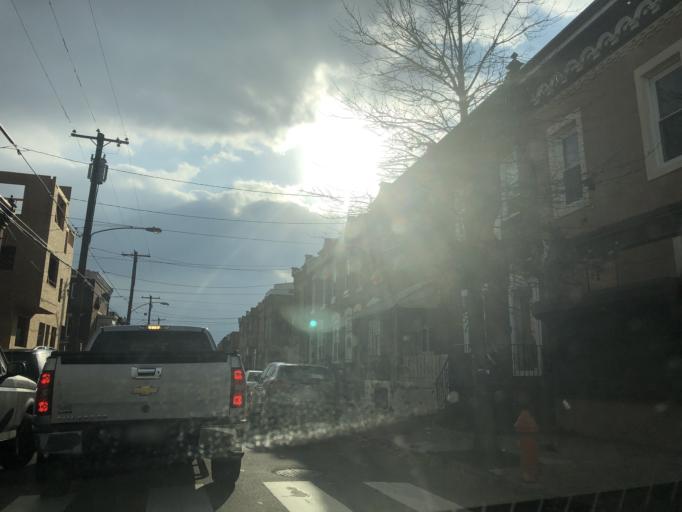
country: US
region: Pennsylvania
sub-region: Philadelphia County
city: Philadelphia
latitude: 39.9278
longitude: -75.1772
